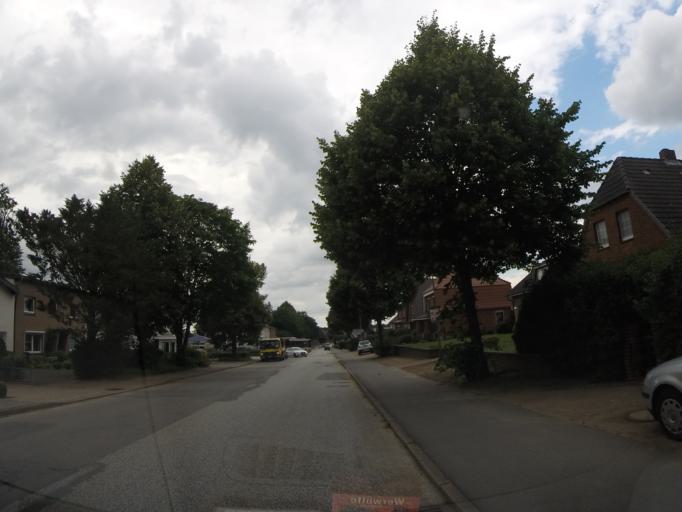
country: DE
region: Schleswig-Holstein
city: Ratekau
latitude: 53.9819
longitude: 10.7131
